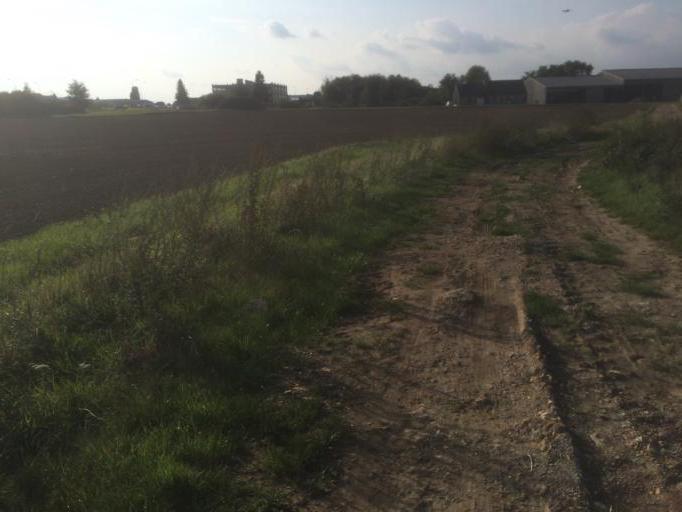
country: FR
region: Ile-de-France
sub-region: Departement des Yvelines
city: Les Loges-en-Josas
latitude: 48.7506
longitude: 2.1234
